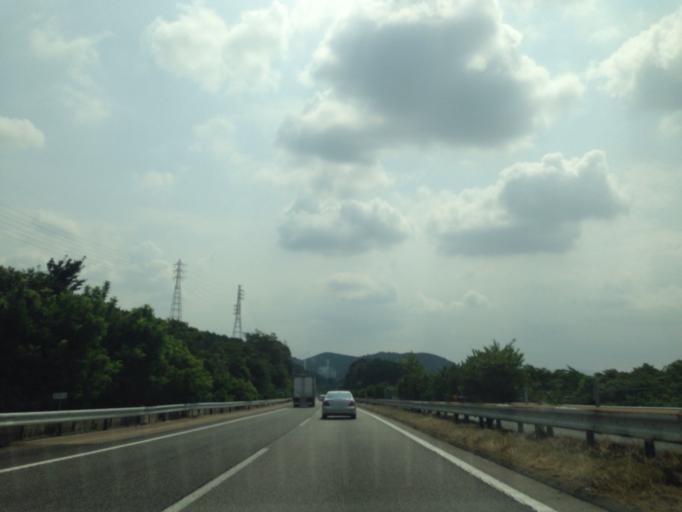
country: JP
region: Aichi
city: Kozakai-cho
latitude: 34.8559
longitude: 137.3350
